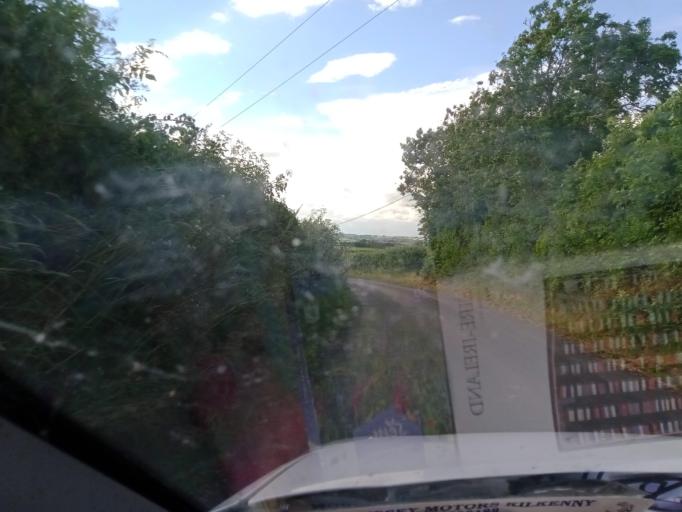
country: IE
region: Leinster
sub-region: Laois
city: Rathdowney
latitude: 52.7734
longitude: -7.5163
